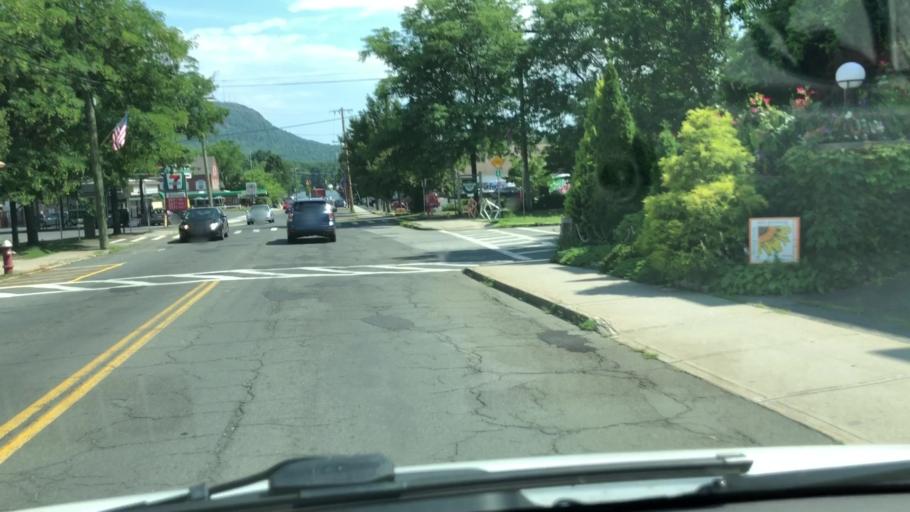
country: US
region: Massachusetts
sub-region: Hampshire County
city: Easthampton
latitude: 42.2676
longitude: -72.6705
